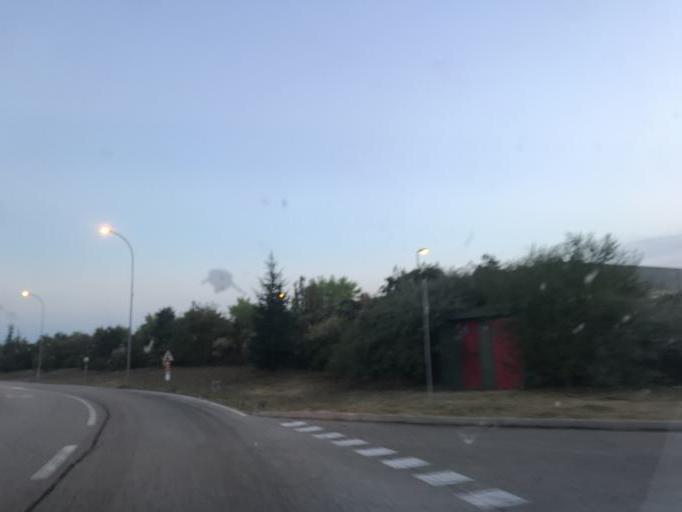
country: FR
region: Rhone-Alpes
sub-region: Departement de l'Isere
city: Hieres-sur-Amby
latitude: 45.8467
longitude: 5.2797
